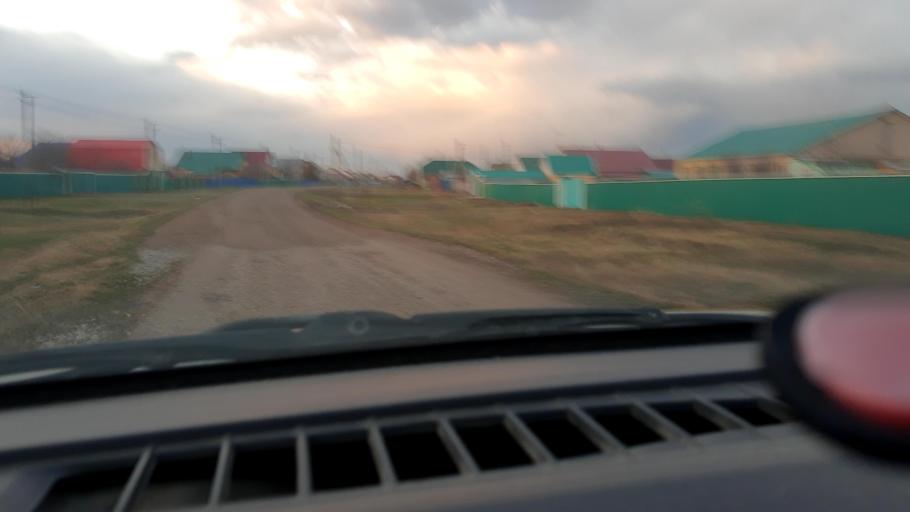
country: RU
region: Bashkortostan
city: Asanovo
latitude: 54.9041
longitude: 55.4846
